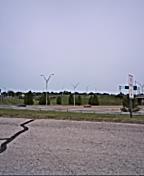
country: US
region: Kentucky
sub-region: Jefferson County
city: Audubon Park
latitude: 38.1887
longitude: -85.7403
